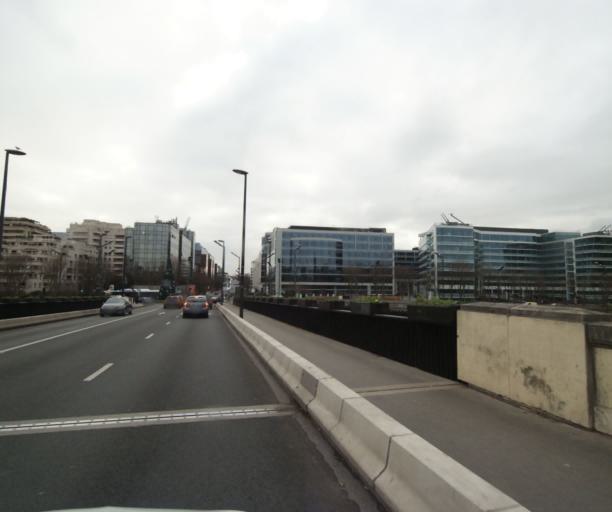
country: FR
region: Ile-de-France
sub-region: Departement des Hauts-de-Seine
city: Levallois-Perret
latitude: 48.8996
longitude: 2.2780
